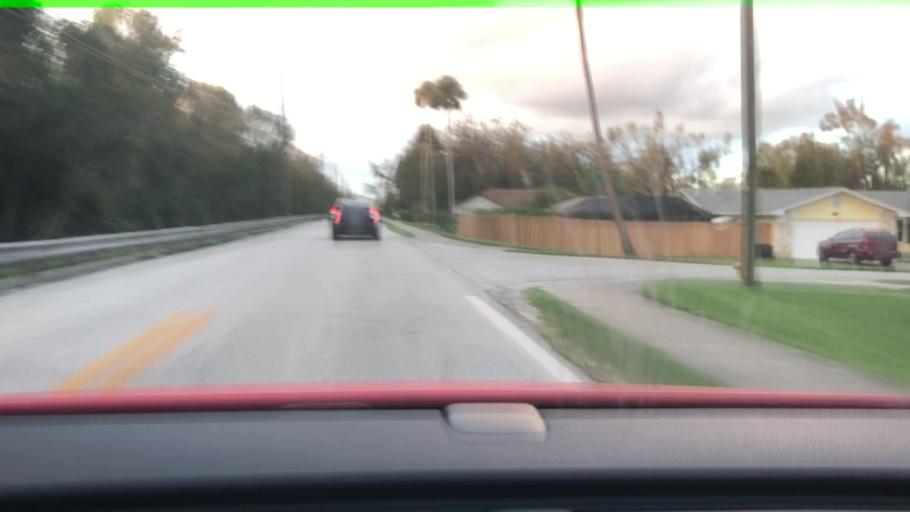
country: US
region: Florida
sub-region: Volusia County
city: South Daytona
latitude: 29.1573
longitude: -81.0129
